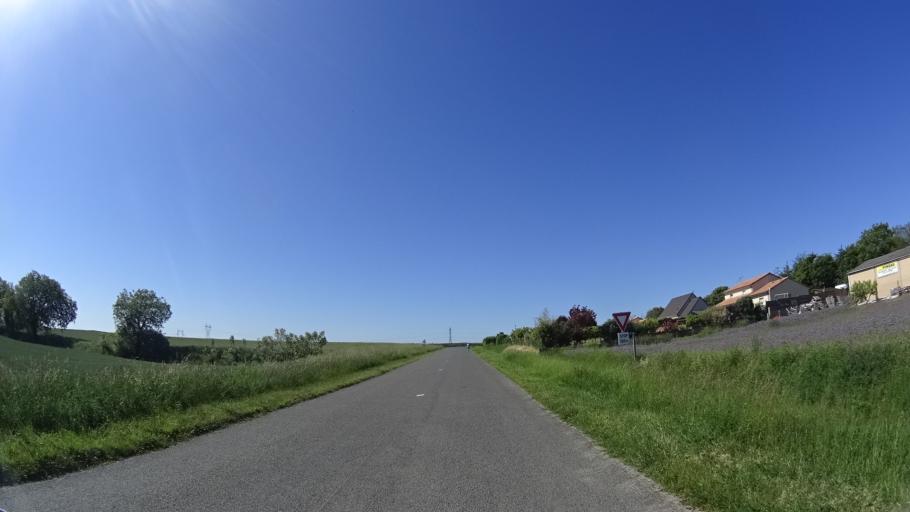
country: FR
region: Pays de la Loire
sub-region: Departement de Maine-et-Loire
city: Doue-la-Fontaine
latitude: 47.2336
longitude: -0.2918
